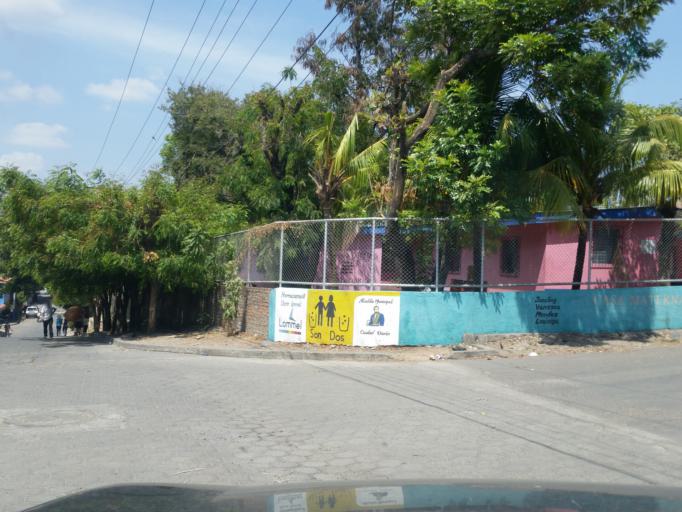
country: NI
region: Matagalpa
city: Ciudad Dario
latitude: 12.7275
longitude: -86.1237
